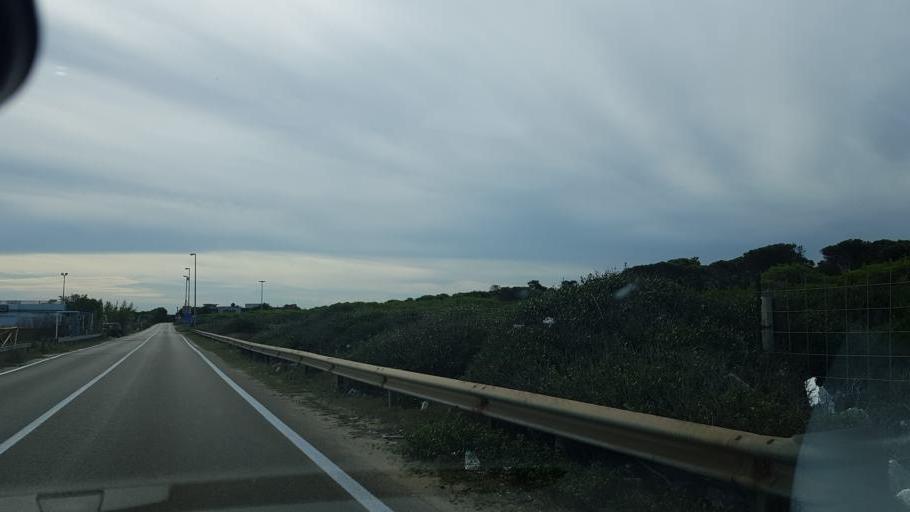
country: IT
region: Apulia
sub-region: Provincia di Lecce
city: Melendugno
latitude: 40.3307
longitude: 18.3721
